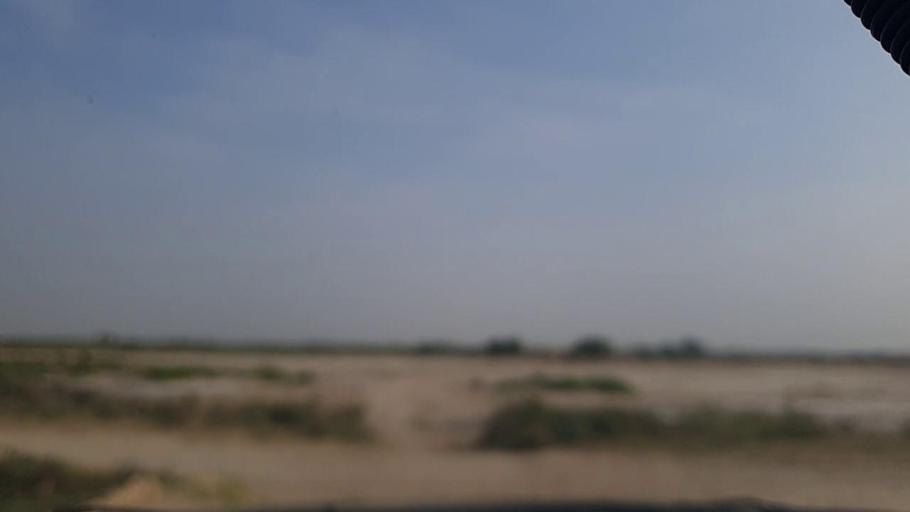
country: PK
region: Sindh
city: Thatta
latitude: 24.7257
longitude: 67.9028
